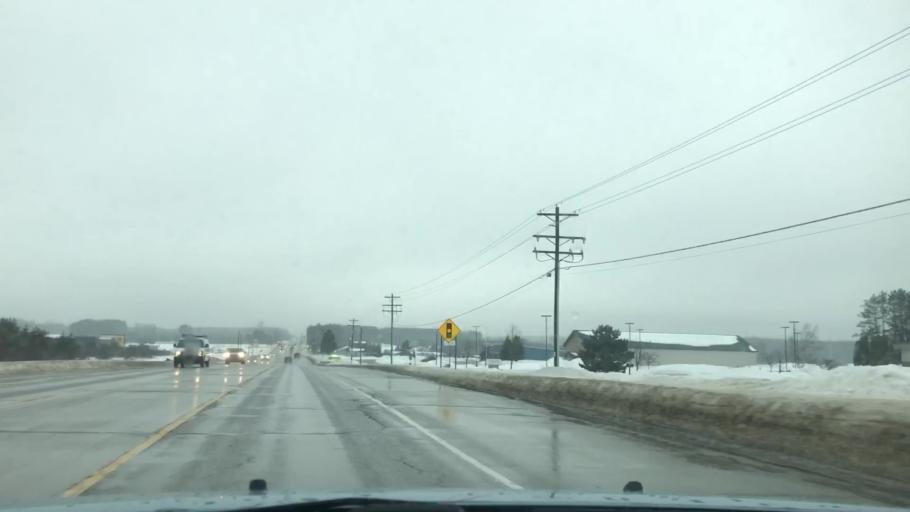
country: US
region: Michigan
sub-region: Otsego County
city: Gaylord
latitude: 45.0275
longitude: -84.7163
